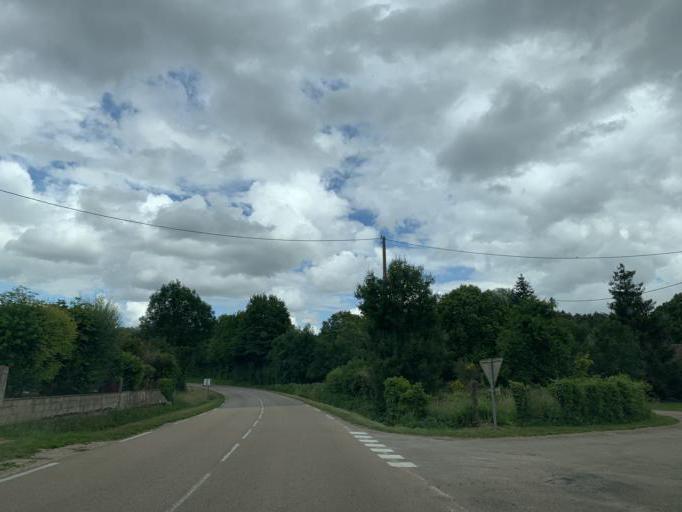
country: FR
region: Bourgogne
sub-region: Departement de l'Yonne
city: Chablis
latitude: 47.7331
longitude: 3.8004
